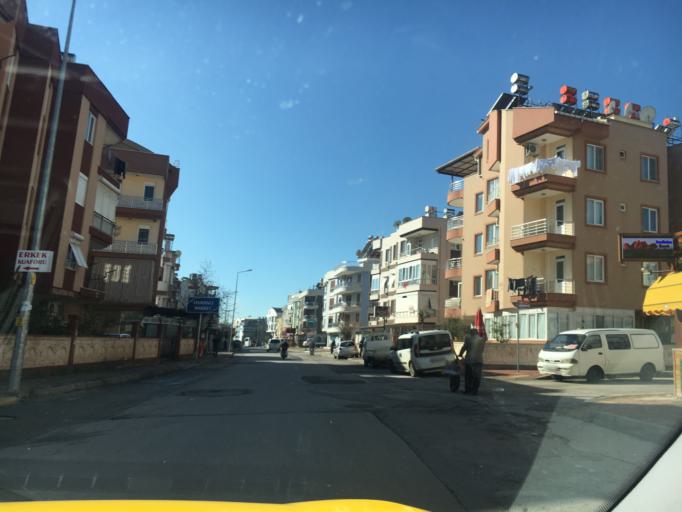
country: TR
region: Antalya
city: Antalya
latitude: 36.9149
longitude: 30.7063
